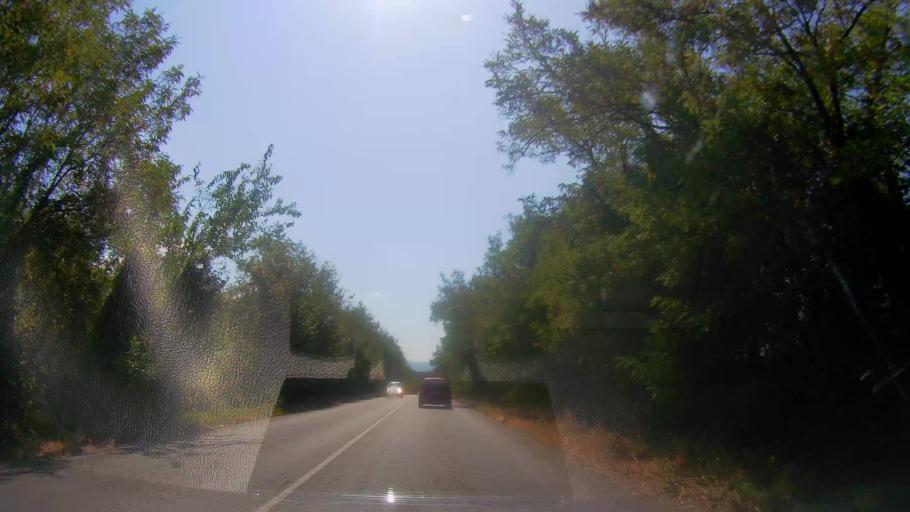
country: BG
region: Veliko Turnovo
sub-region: Obshtina Gorna Oryakhovitsa
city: Purvomaytsi
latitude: 43.2536
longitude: 25.6431
